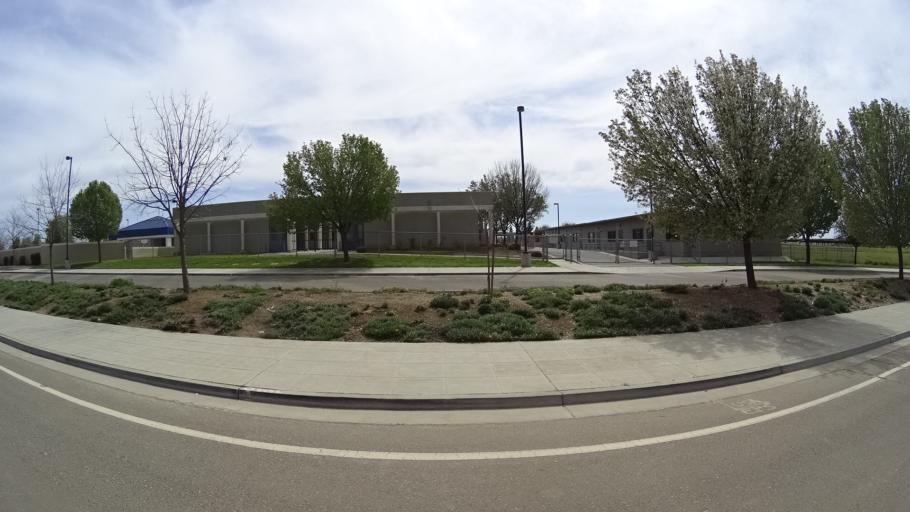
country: US
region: California
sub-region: Fresno County
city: Biola
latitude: 36.8007
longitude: -119.9094
